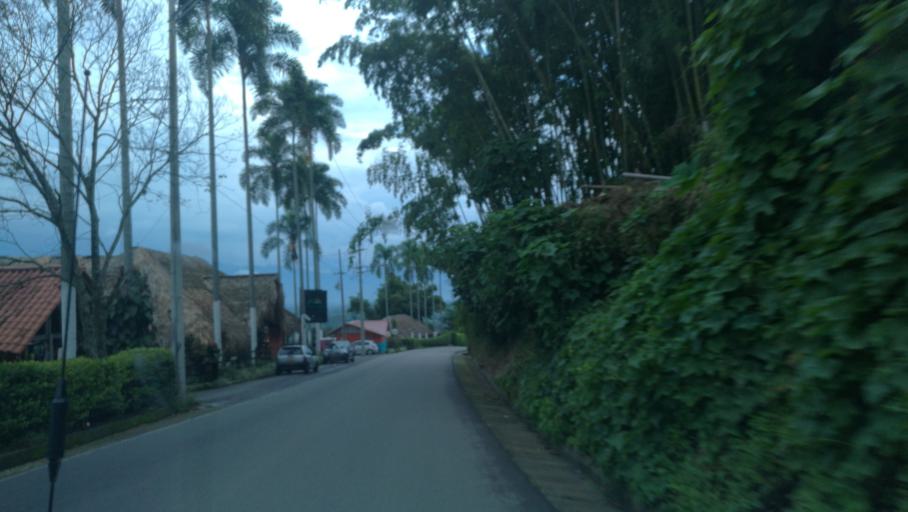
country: CO
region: Quindio
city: Montenegro
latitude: 4.5145
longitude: -75.7842
